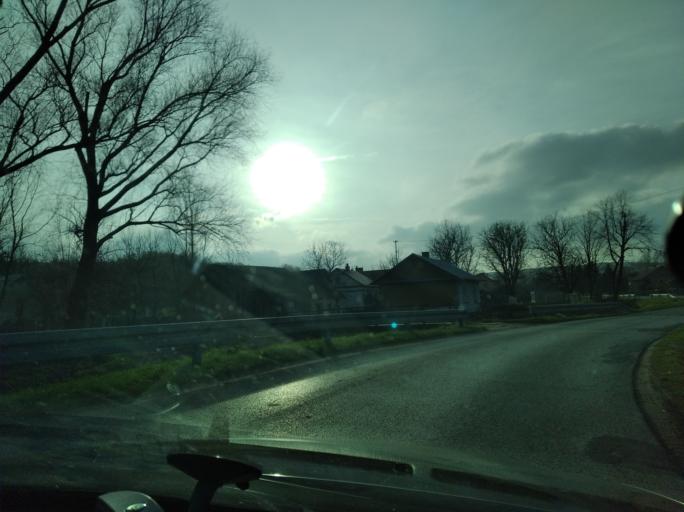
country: PL
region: Subcarpathian Voivodeship
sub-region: Powiat przeworski
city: Lopuszka Wielka
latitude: 49.9392
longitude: 22.4011
